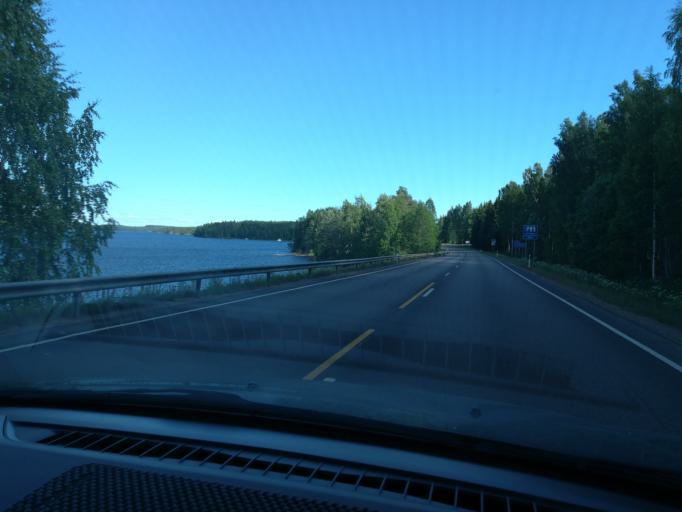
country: FI
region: Southern Savonia
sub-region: Mikkeli
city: Puumala
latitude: 61.5131
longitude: 28.1773
